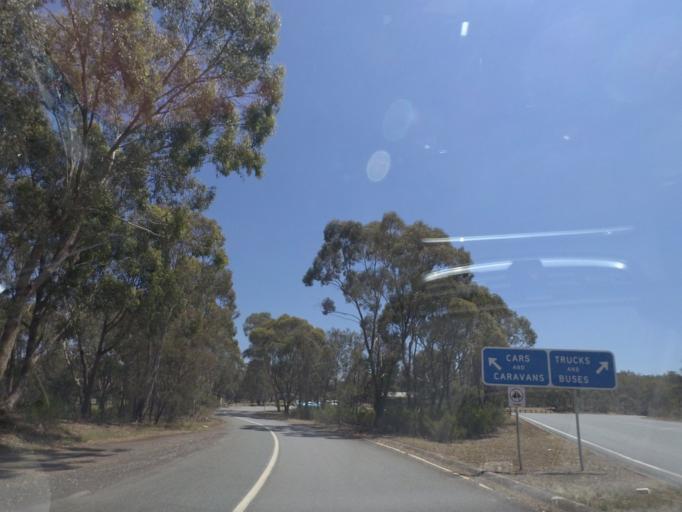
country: AU
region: Victoria
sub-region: Murrindindi
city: Kinglake West
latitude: -36.9638
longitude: 145.1810
